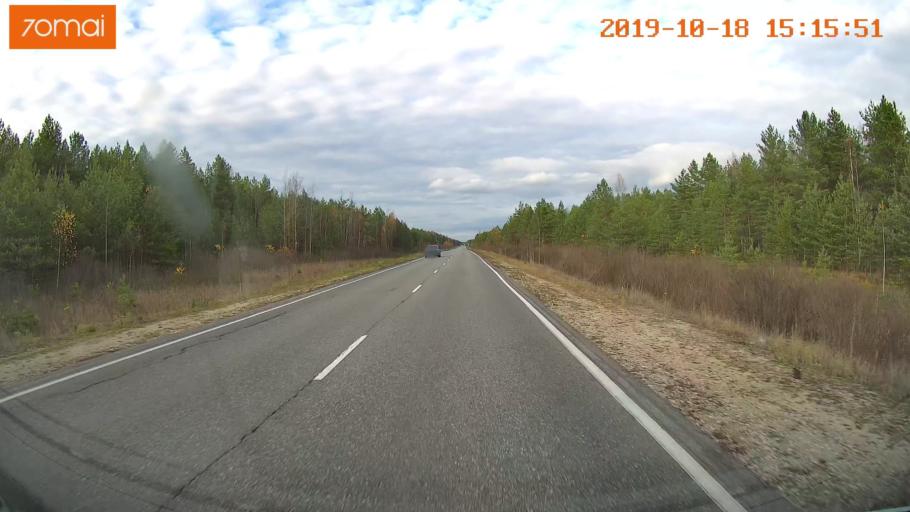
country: RU
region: Vladimir
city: Gus'-Khrustal'nyy
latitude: 55.6260
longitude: 40.7234
